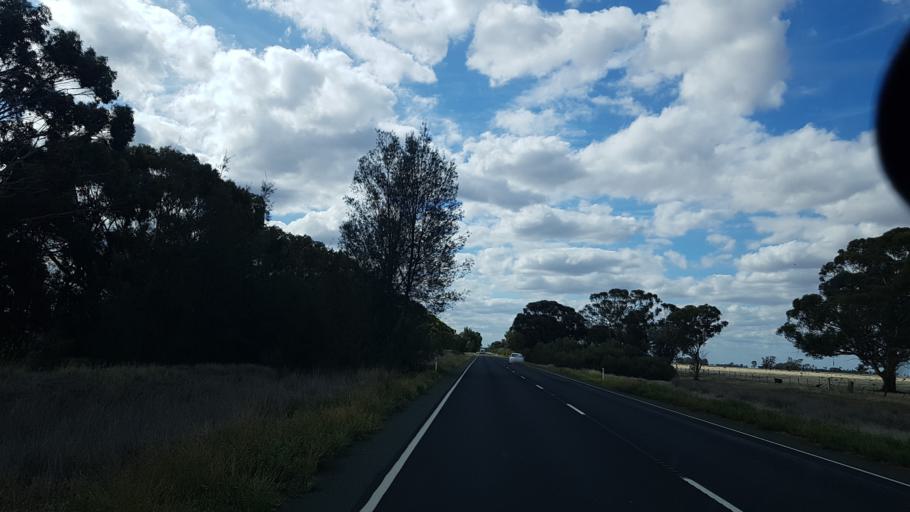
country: AU
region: Victoria
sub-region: Swan Hill
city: Swan Hill
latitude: -35.9819
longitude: 143.9451
